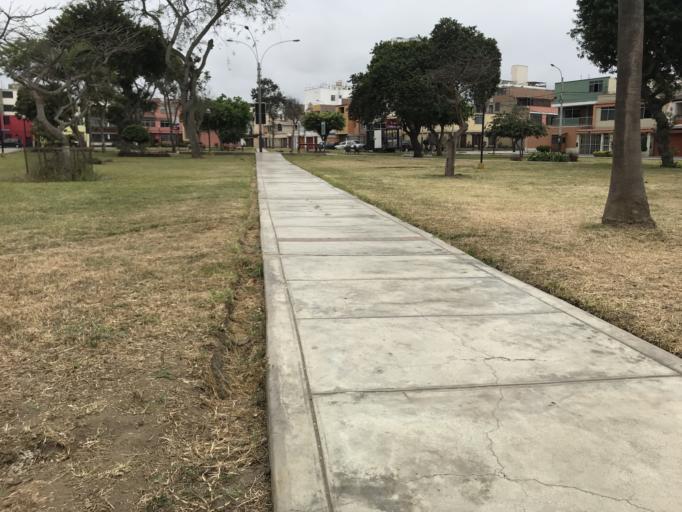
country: PE
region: Lima
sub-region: Lima
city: San Isidro
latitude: -12.0782
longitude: -77.0745
